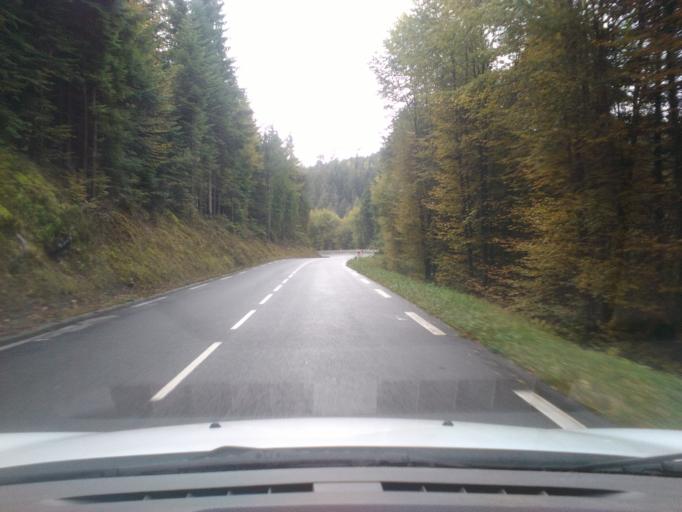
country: FR
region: Lorraine
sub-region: Departement des Vosges
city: Taintrux
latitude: 48.2748
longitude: 6.8468
